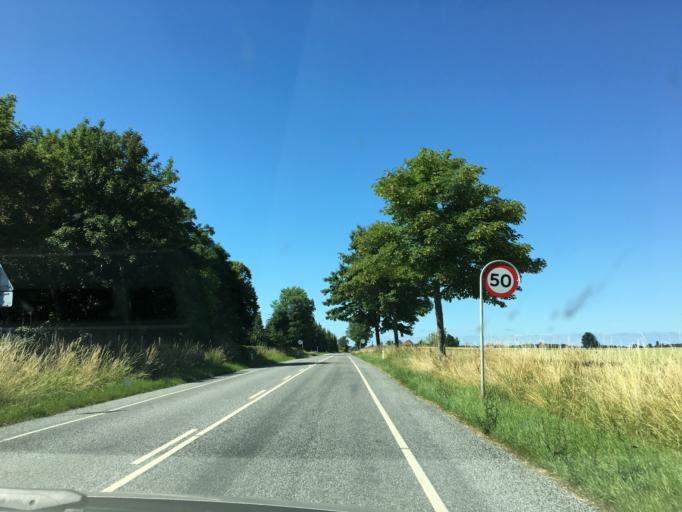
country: DK
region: South Denmark
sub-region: Langeland Kommune
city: Rudkobing
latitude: 54.7721
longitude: 10.7160
